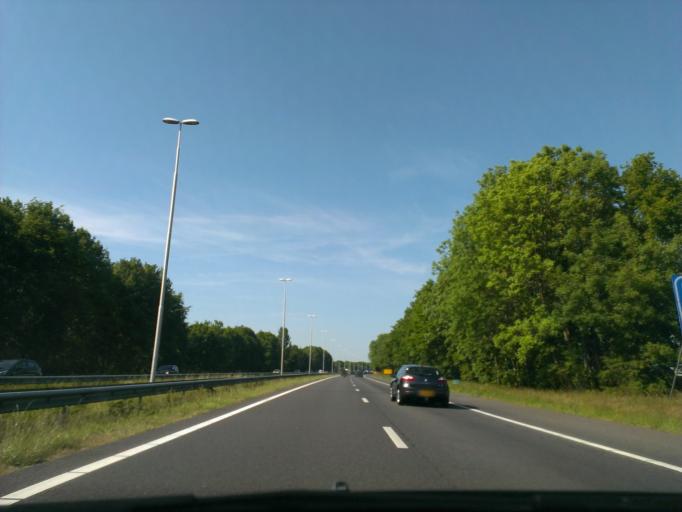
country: NL
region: Gelderland
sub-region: Gemeente Epe
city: Emst
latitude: 52.3215
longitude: 6.0062
